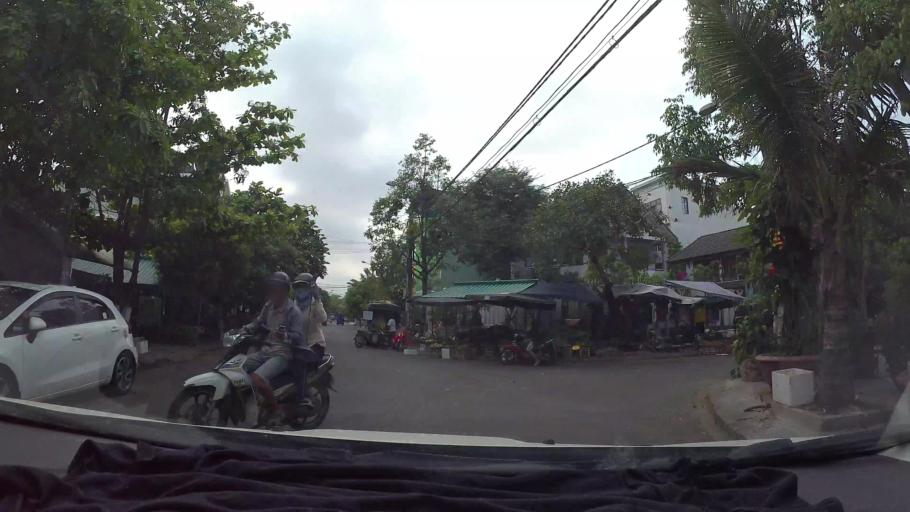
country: VN
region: Da Nang
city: Thanh Khe
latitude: 16.0581
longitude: 108.1770
